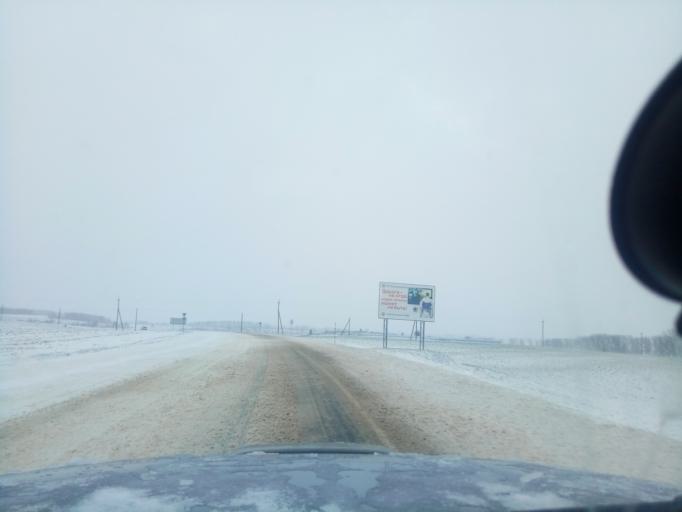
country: BY
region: Minsk
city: Haradzyeya
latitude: 53.3341
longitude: 26.5243
